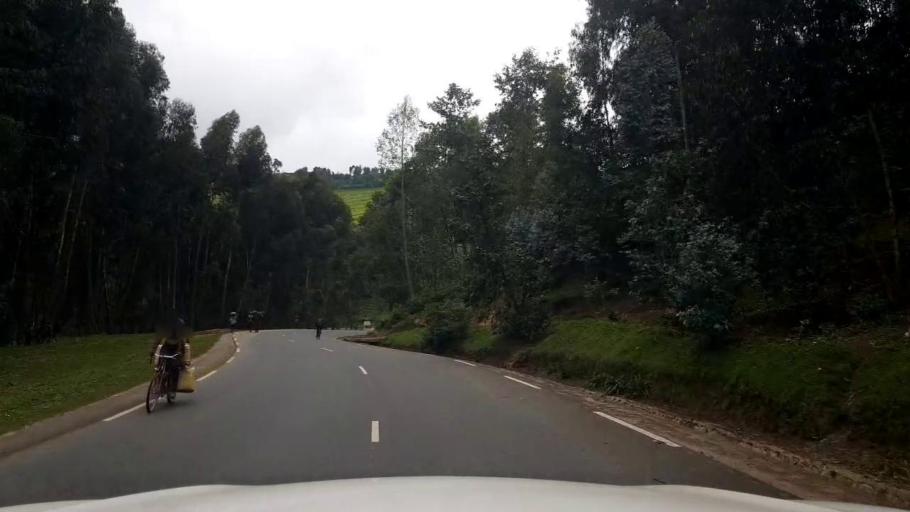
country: RW
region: Northern Province
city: Musanze
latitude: -1.6544
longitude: 29.5103
